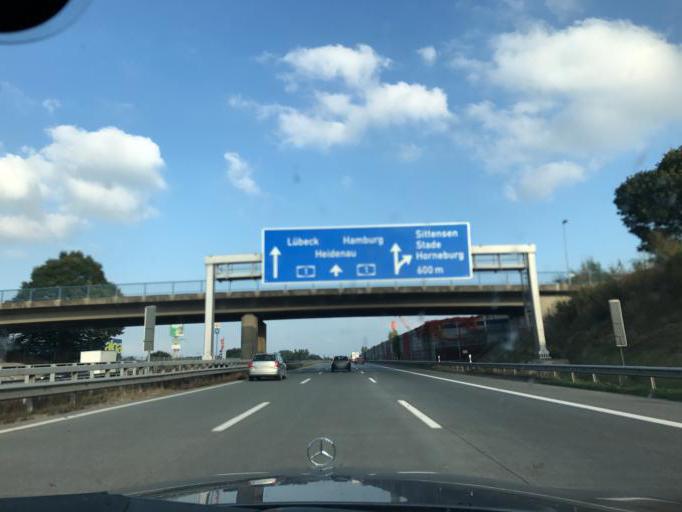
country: DE
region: Lower Saxony
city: Sittensen
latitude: 53.2899
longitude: 9.4985
